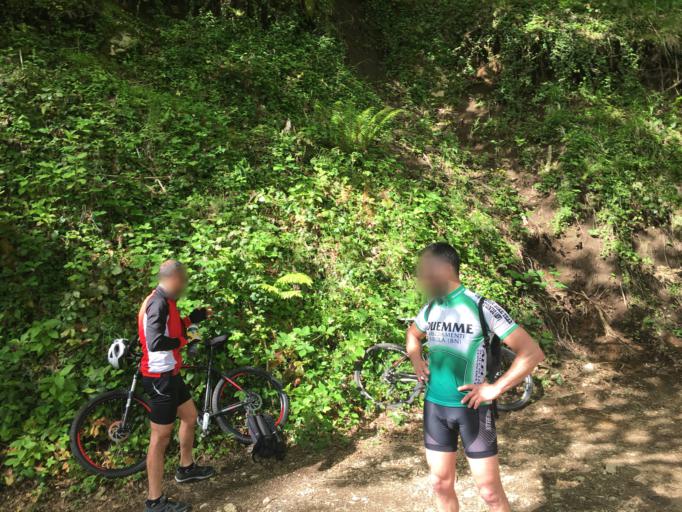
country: IT
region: Campania
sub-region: Provincia di Avellino
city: Cervinara
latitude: 41.0046
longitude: 14.5988
